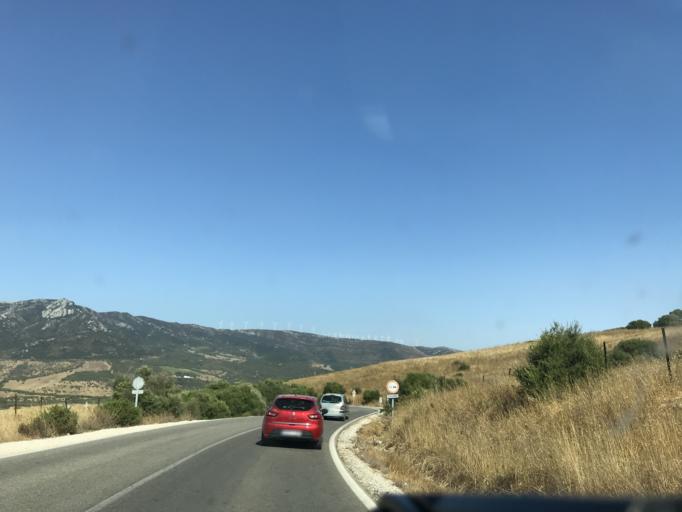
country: ES
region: Andalusia
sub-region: Provincia de Cadiz
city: Zahara de los Atunes
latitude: 36.1025
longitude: -5.7270
